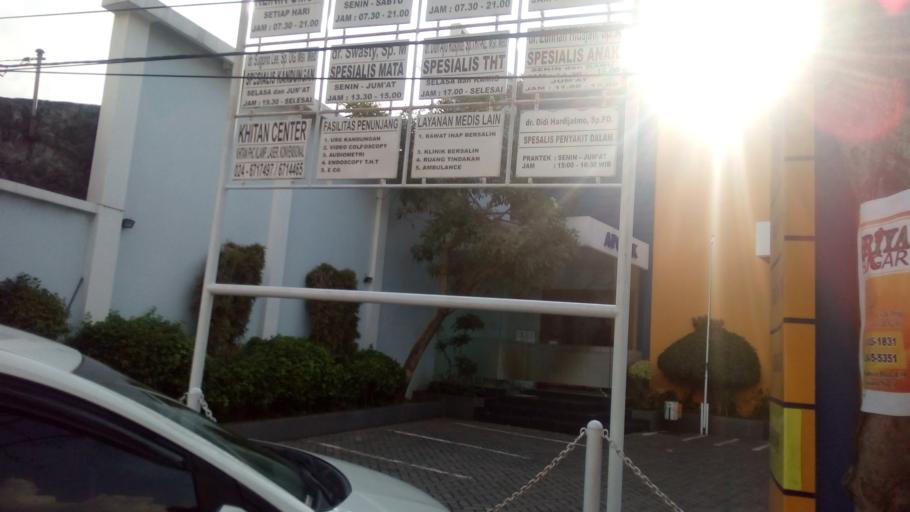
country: ID
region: Central Java
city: Mranggen
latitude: -7.0048
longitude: 110.4705
